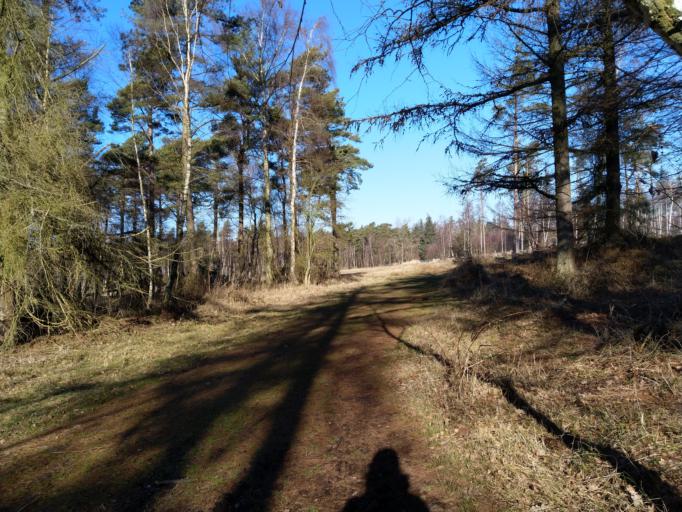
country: DK
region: Zealand
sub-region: Guldborgsund Kommune
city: Nykobing Falster
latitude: 54.6426
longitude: 11.9571
